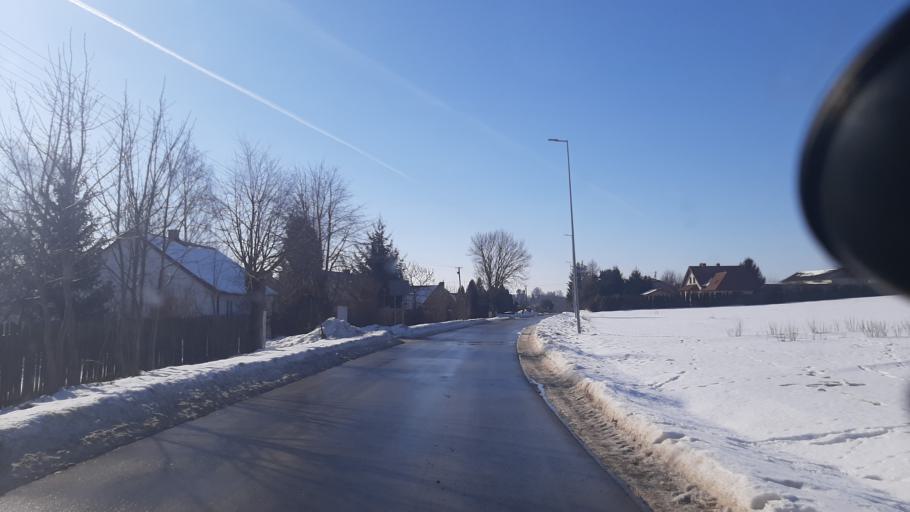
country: PL
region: Lublin Voivodeship
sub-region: Powiat lubelski
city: Garbow
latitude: 51.2960
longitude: 22.3036
